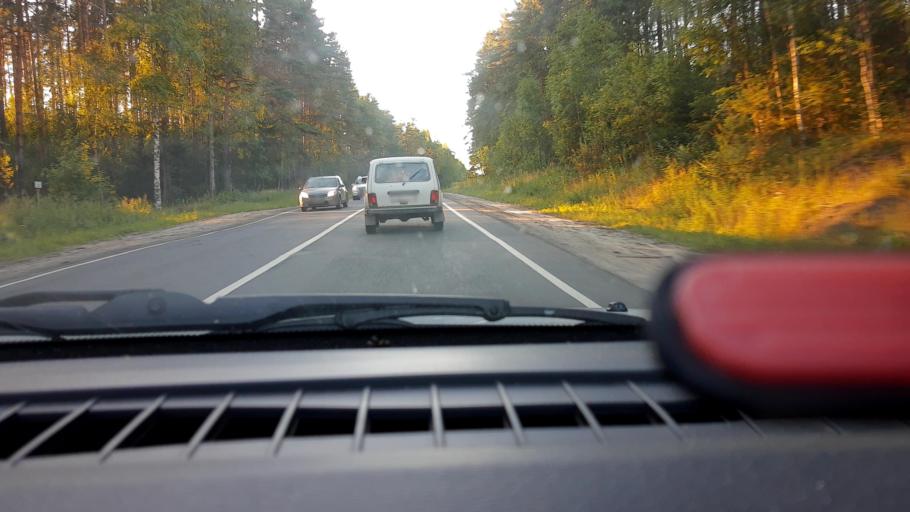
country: RU
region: Nizjnij Novgorod
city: Krasnyye Baki
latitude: 56.9909
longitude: 45.1159
